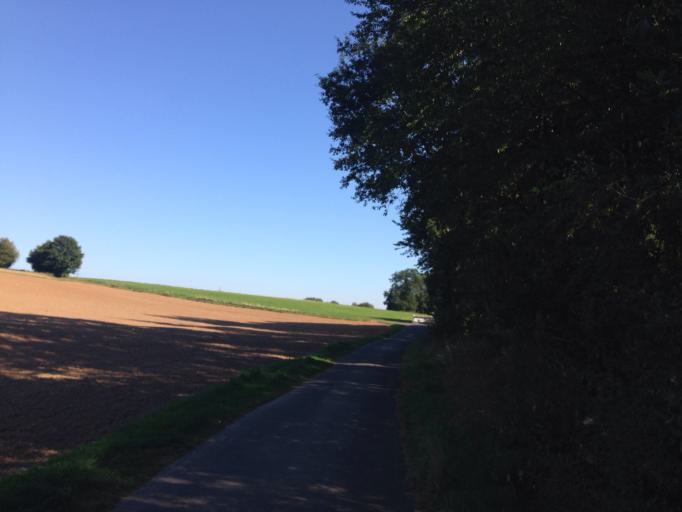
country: DE
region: Hesse
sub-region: Regierungsbezirk Giessen
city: Grunberg
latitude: 50.6195
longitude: 8.9469
